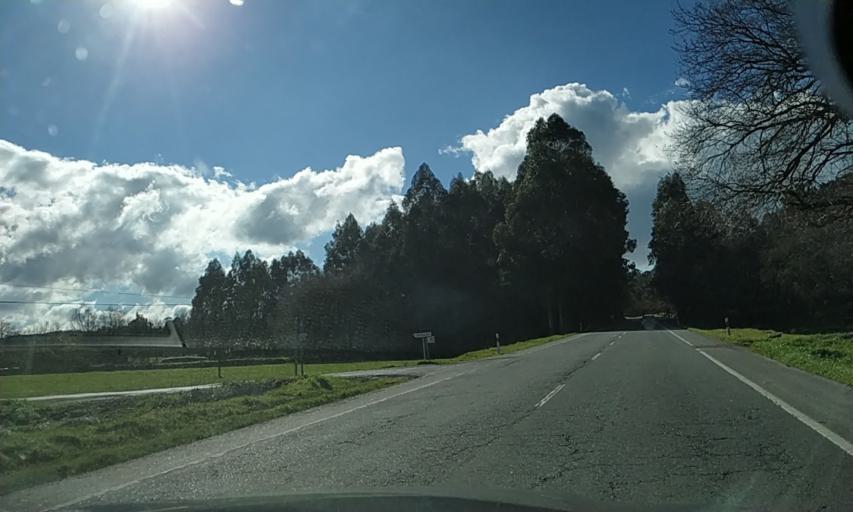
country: ES
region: Galicia
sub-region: Provincia de Pontevedra
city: Silleda
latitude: 42.7059
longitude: -8.3048
